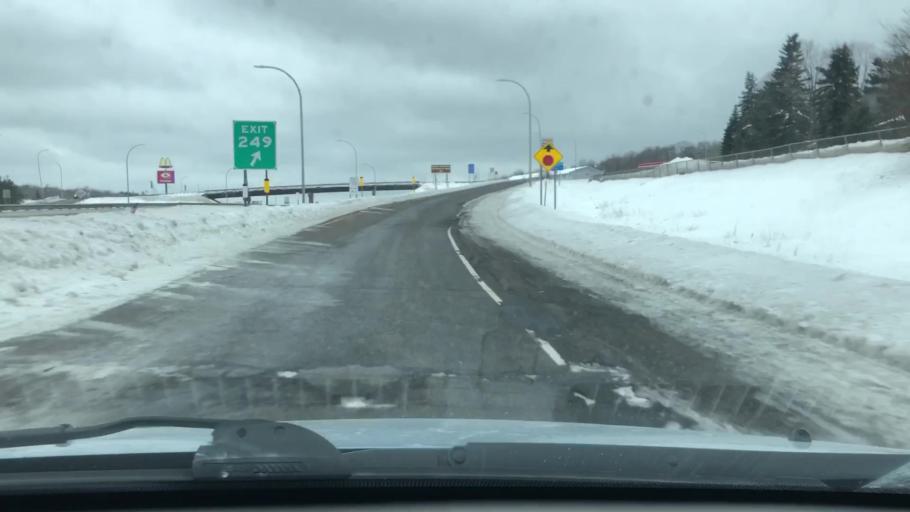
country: US
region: Minnesota
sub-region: Saint Louis County
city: Proctor
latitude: 46.7263
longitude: -92.2140
